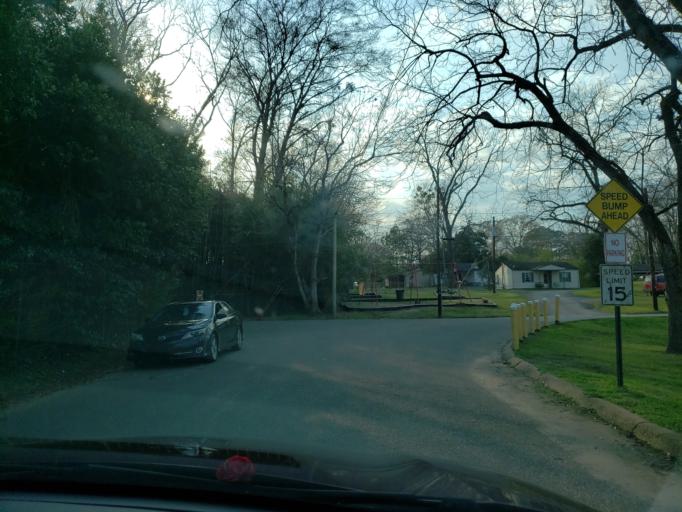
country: US
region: Alabama
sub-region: Hale County
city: Greensboro
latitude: 32.7053
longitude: -87.5988
